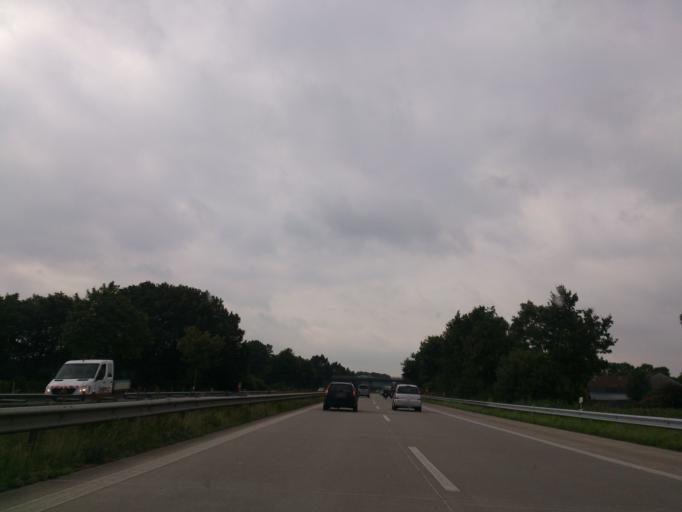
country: DE
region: Schleswig-Holstein
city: Klein Offenseth-Sparrieshoop
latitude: 53.7804
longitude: 9.7050
